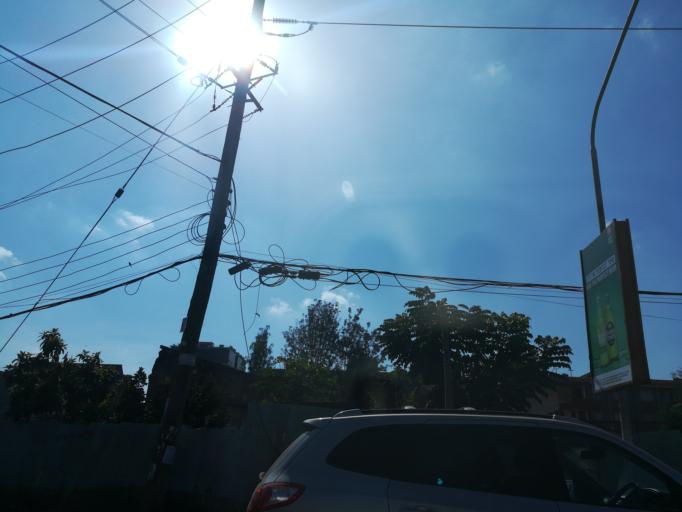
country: KE
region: Nairobi Area
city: Nairobi
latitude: -1.2954
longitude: 36.7877
